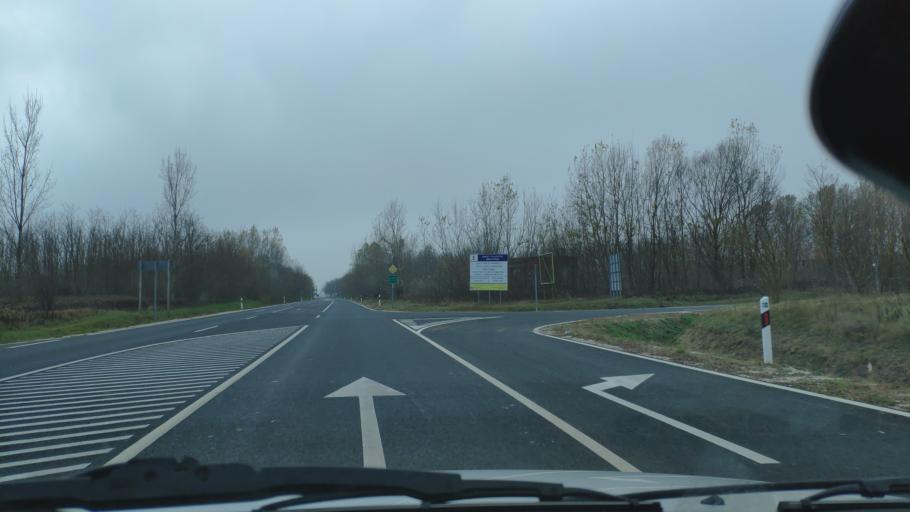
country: HU
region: Zala
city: Zalakomar
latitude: 46.6046
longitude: 17.2683
